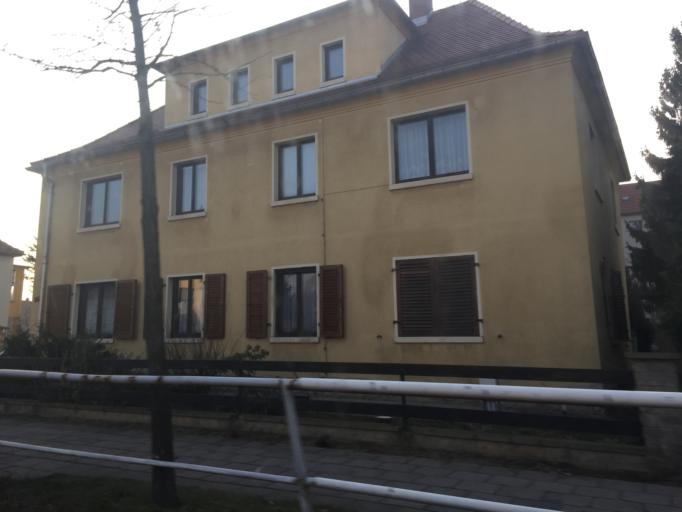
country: DE
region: Saxony
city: Pirna
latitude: 50.9717
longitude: 13.9316
